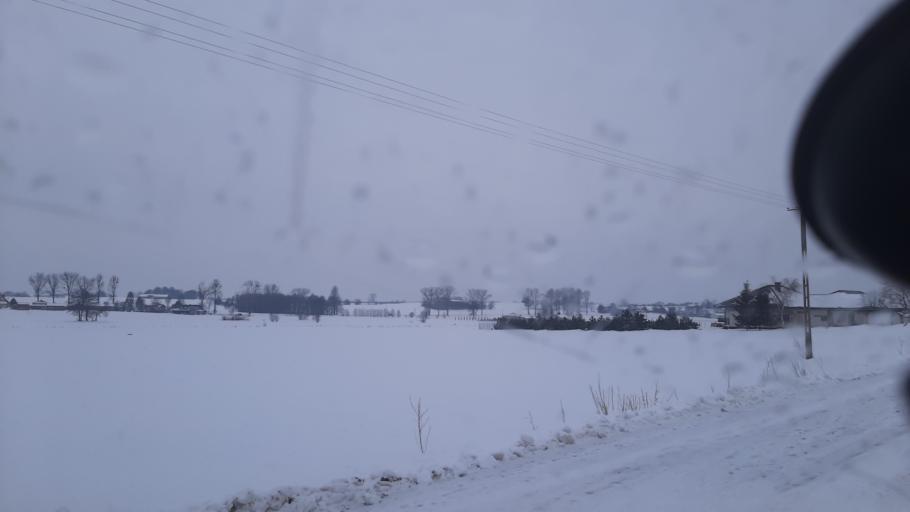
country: PL
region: Lublin Voivodeship
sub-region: Powiat lubelski
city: Jastkow
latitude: 51.3498
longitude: 22.3999
